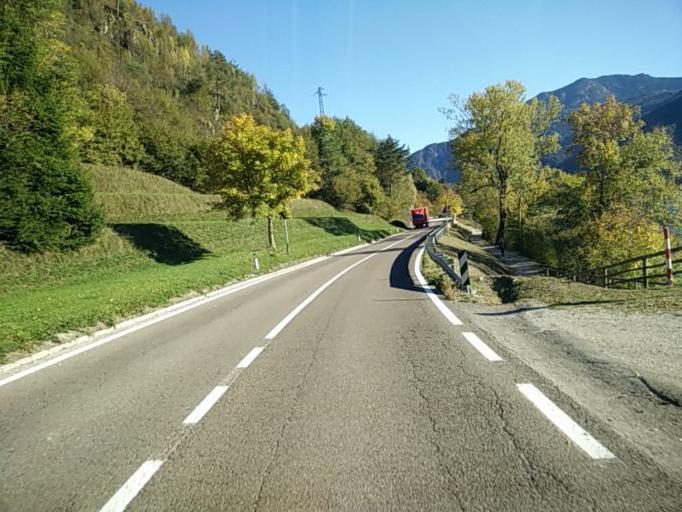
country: IT
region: Trentino-Alto Adige
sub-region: Provincia di Trento
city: Pieve di Ledro
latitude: 45.8845
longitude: 10.7464
